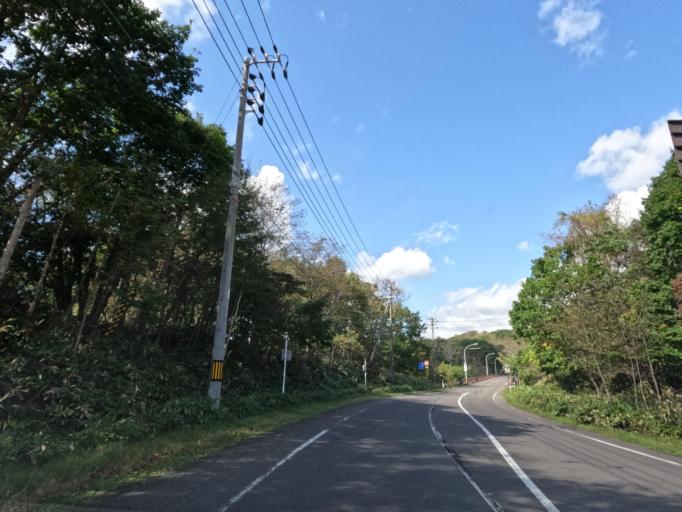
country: JP
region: Hokkaido
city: Shiraoi
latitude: 42.4738
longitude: 141.1474
